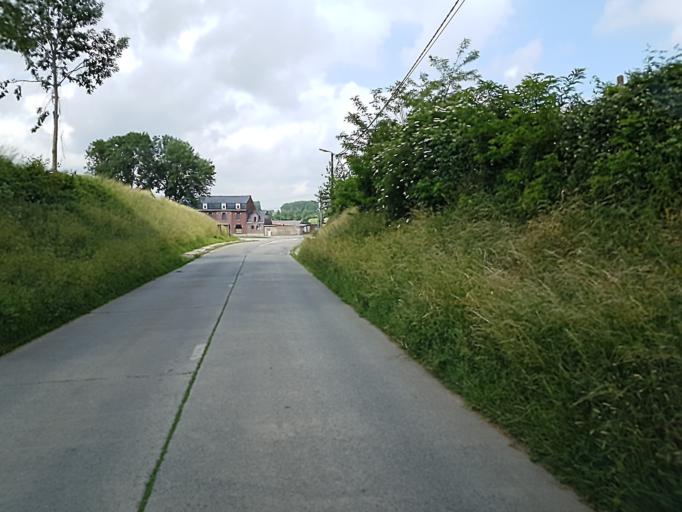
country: BE
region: Flanders
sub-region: Provincie Vlaams-Brabant
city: Herne
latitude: 50.7281
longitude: 4.0866
